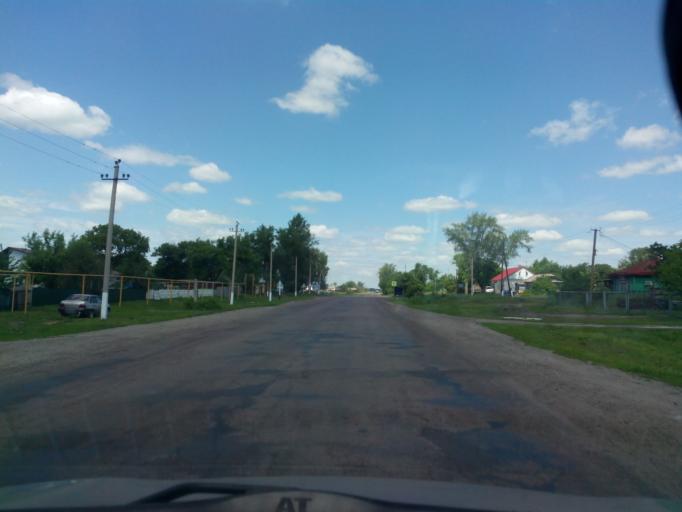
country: RU
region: Tambov
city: Zherdevka
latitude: 51.7540
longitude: 41.5119
